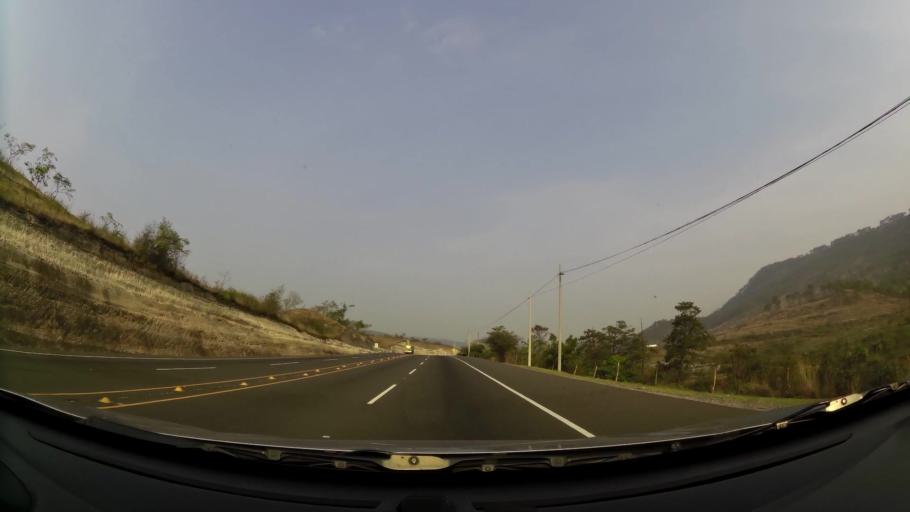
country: HN
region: Francisco Morazan
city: Zambrano
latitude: 14.2331
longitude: -87.3841
